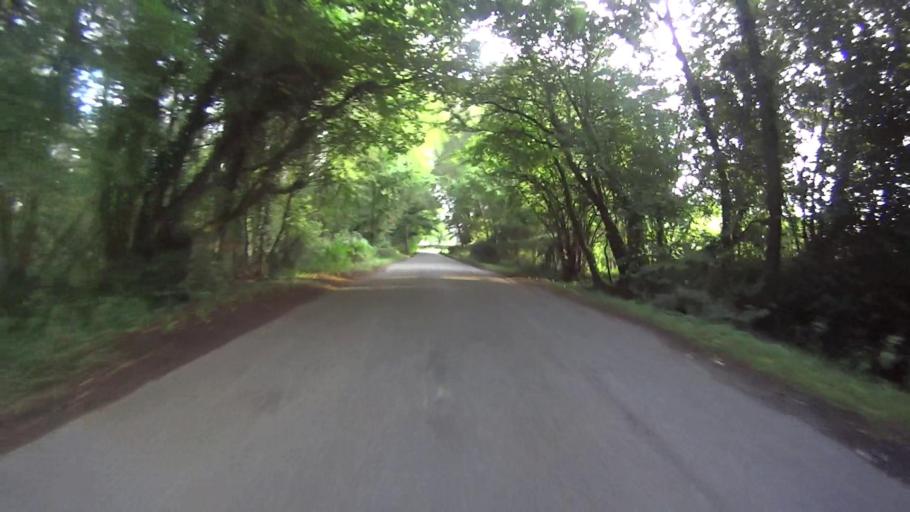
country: GB
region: England
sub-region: West Sussex
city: Copthorne
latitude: 51.1216
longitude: -0.1291
